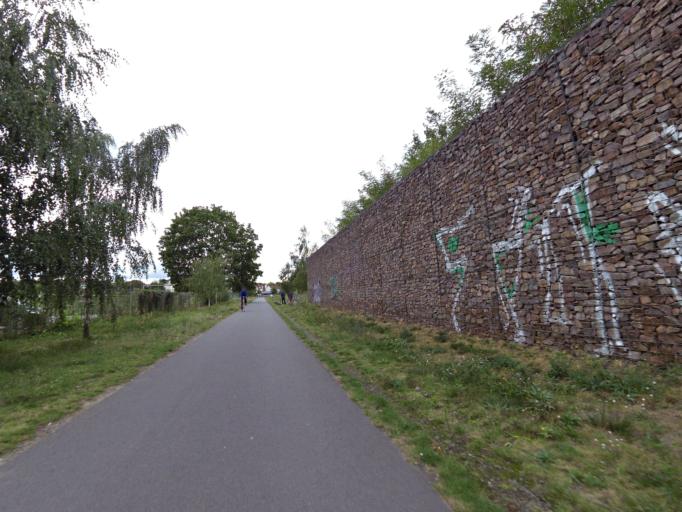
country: DE
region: Berlin
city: Johannisthal
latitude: 52.4406
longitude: 13.5107
